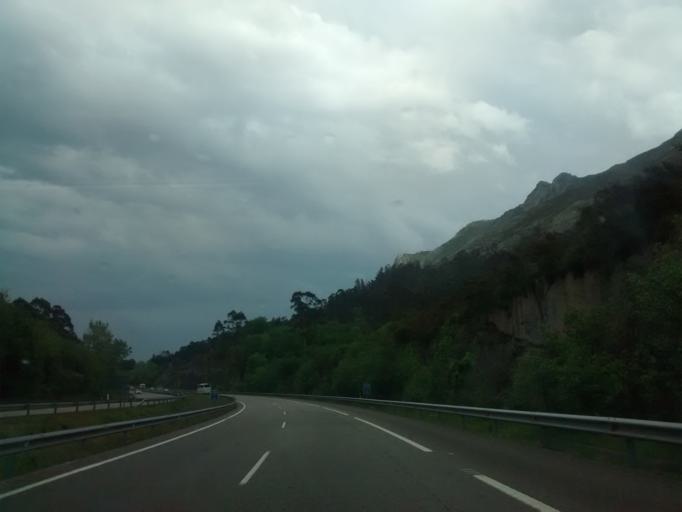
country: ES
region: Asturias
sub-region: Province of Asturias
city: Ribadesella
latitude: 43.4347
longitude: -4.9978
